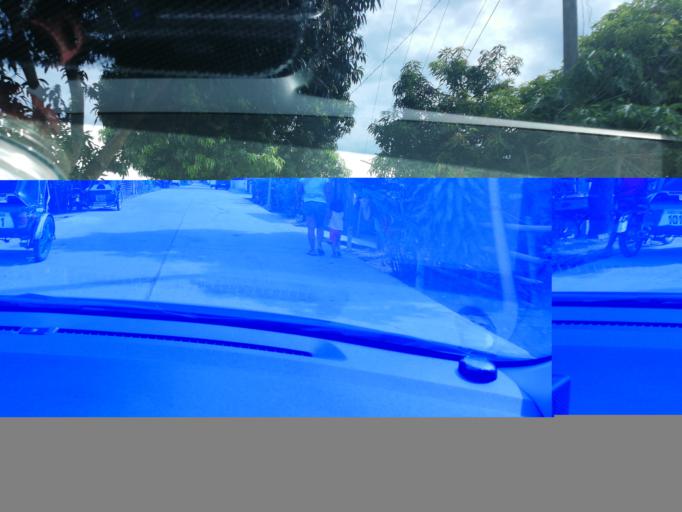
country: PH
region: Ilocos
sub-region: Province of Ilocos Sur
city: Santiago
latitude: 17.2908
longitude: 120.4371
